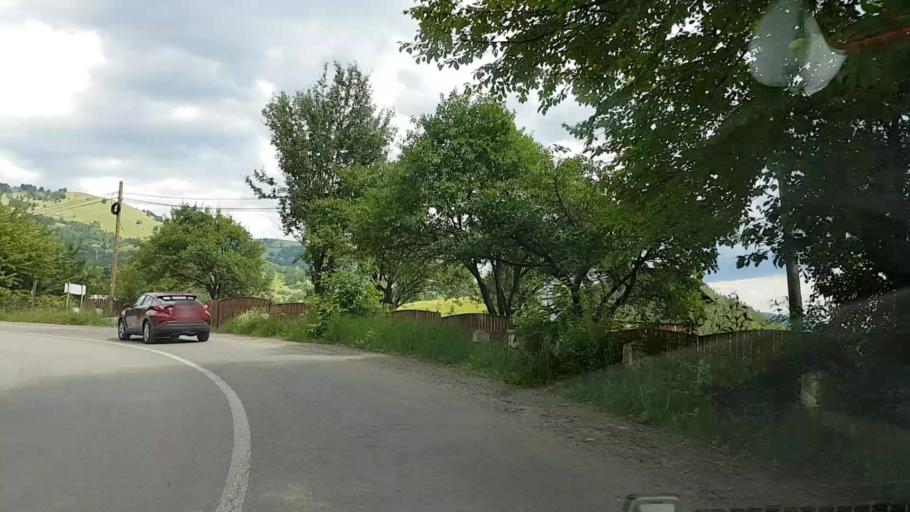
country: RO
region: Neamt
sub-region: Comuna Hangu
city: Hangu
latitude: 47.0456
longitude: 26.0424
